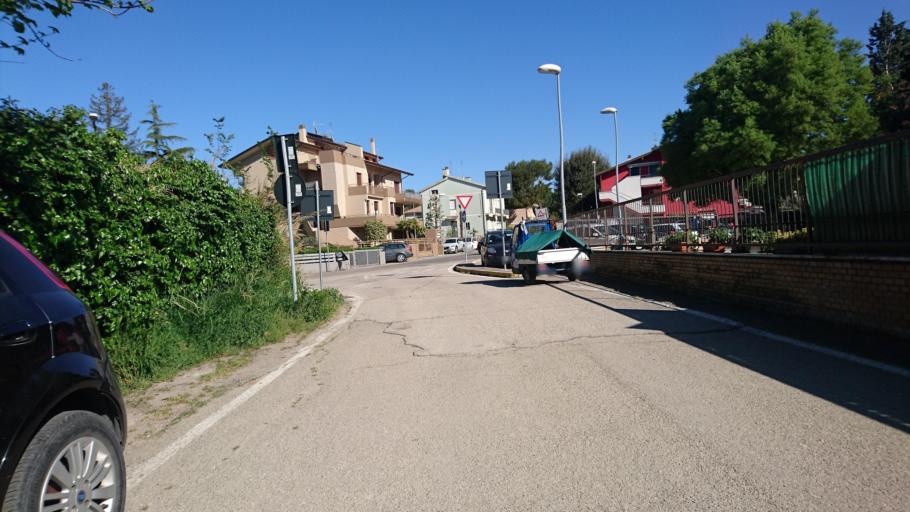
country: IT
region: The Marches
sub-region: Provincia di Pesaro e Urbino
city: Pesaro
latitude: 43.8987
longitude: 12.8953
